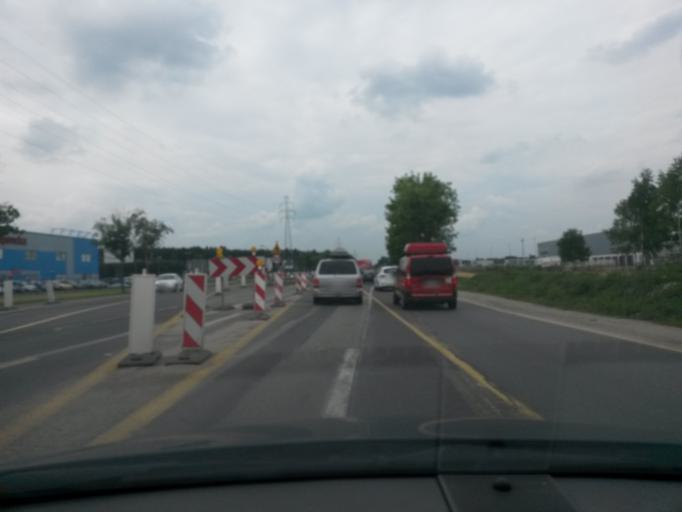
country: PL
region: Masovian Voivodeship
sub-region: Powiat pruszkowski
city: Nadarzyn
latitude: 52.1035
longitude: 20.8302
